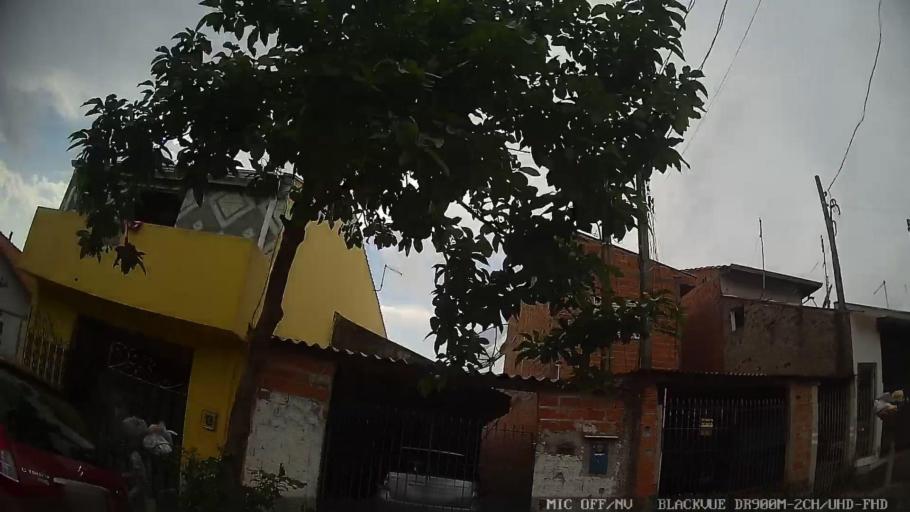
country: BR
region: Sao Paulo
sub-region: Indaiatuba
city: Indaiatuba
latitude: -23.1187
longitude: -47.2457
